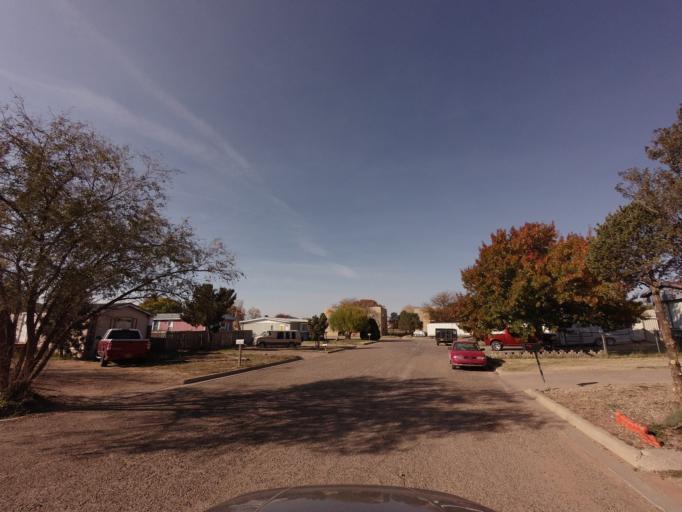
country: US
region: New Mexico
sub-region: Curry County
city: Clovis
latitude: 34.4074
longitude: -103.1745
